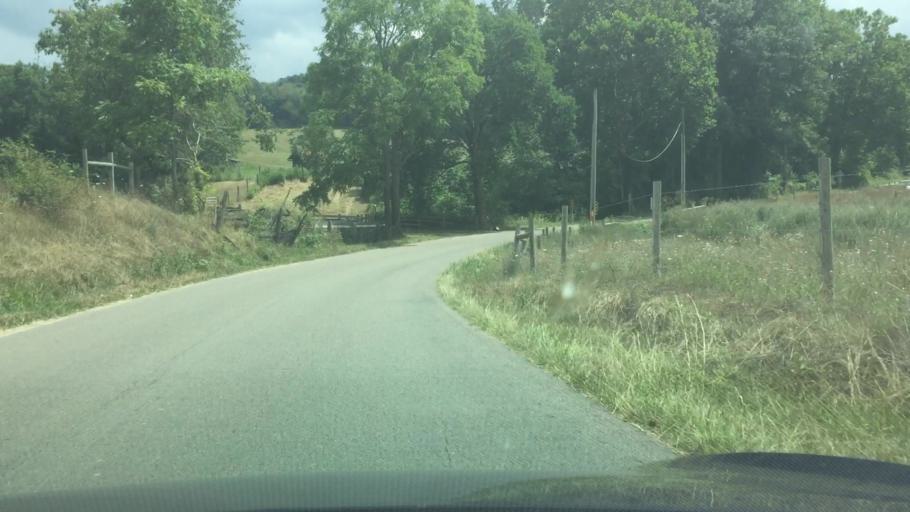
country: US
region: Virginia
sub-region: Wythe County
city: Wytheville
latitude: 36.9362
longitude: -81.0265
